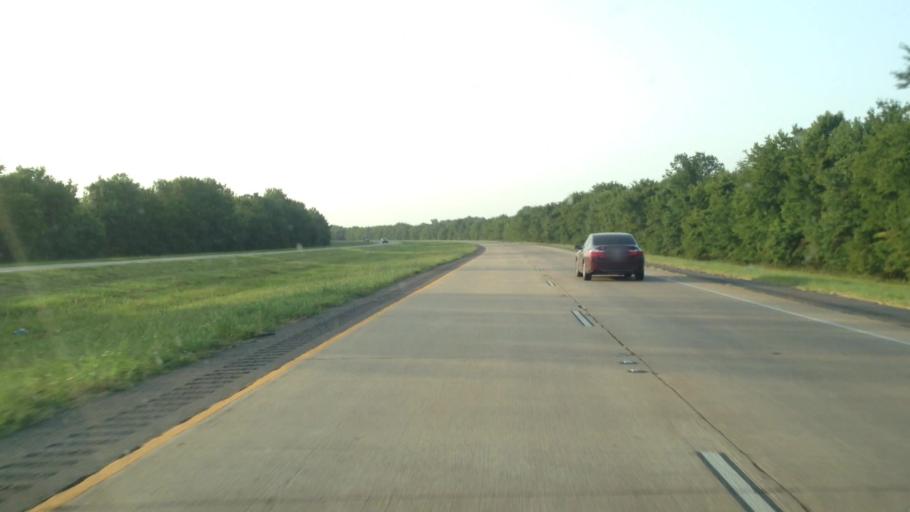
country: US
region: Louisiana
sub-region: Natchitoches Parish
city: Vienna Bend
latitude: 31.5786
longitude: -93.0227
